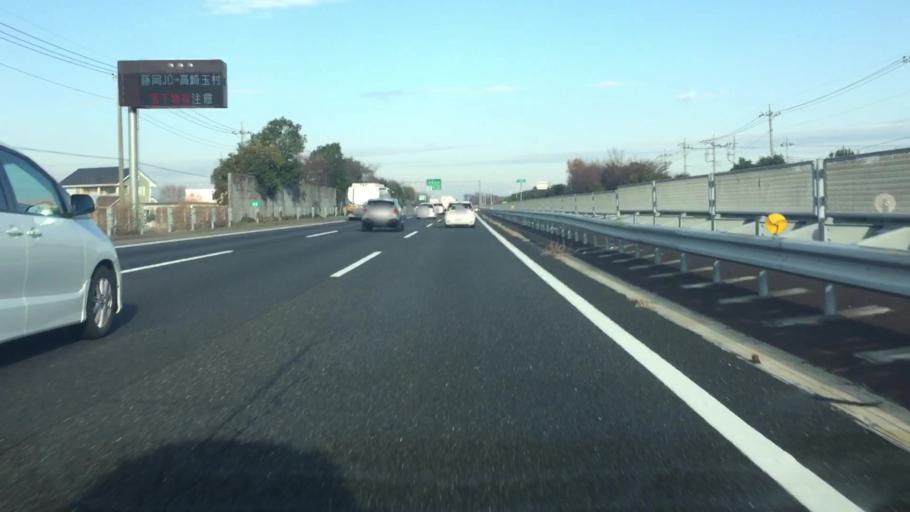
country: JP
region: Saitama
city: Honjo
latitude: 36.2133
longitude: 139.1679
